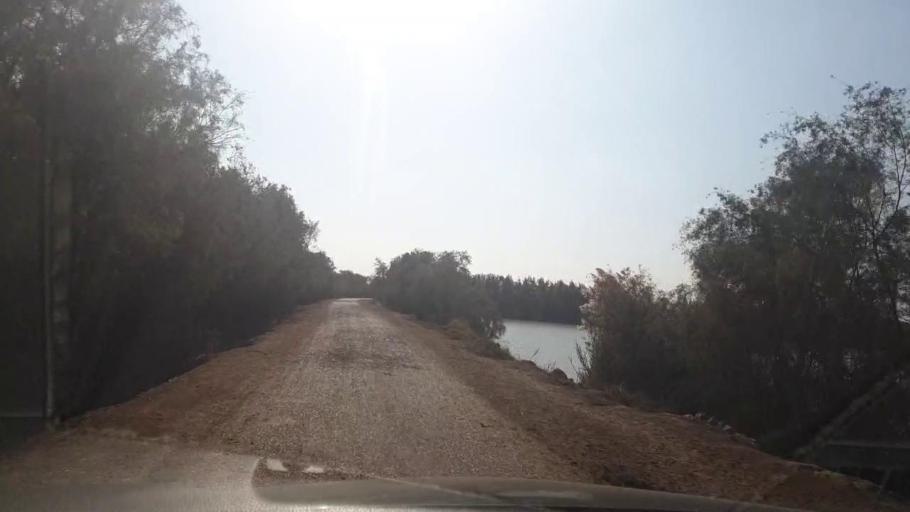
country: PK
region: Sindh
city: Khairpur
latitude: 28.1401
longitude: 69.6019
